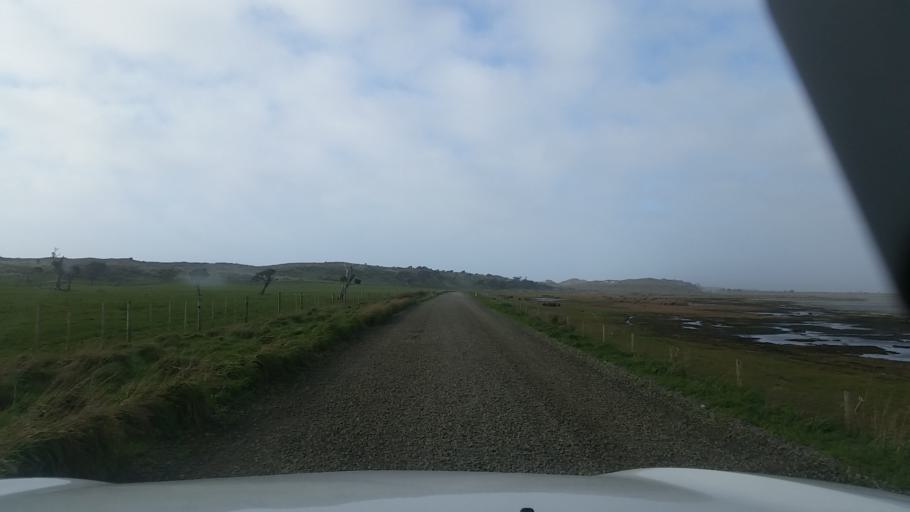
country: NZ
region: Chatham Islands
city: Waitangi
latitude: -43.7499
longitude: -176.4492
